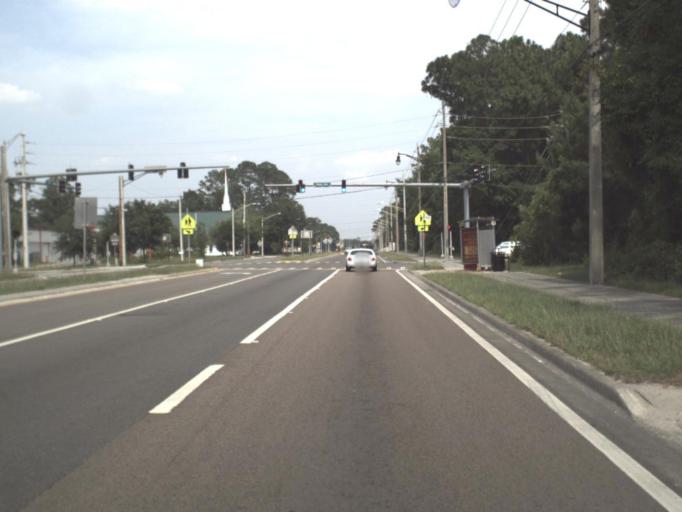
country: US
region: Florida
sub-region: Clay County
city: Bellair-Meadowbrook Terrace
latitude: 30.2474
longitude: -81.8243
